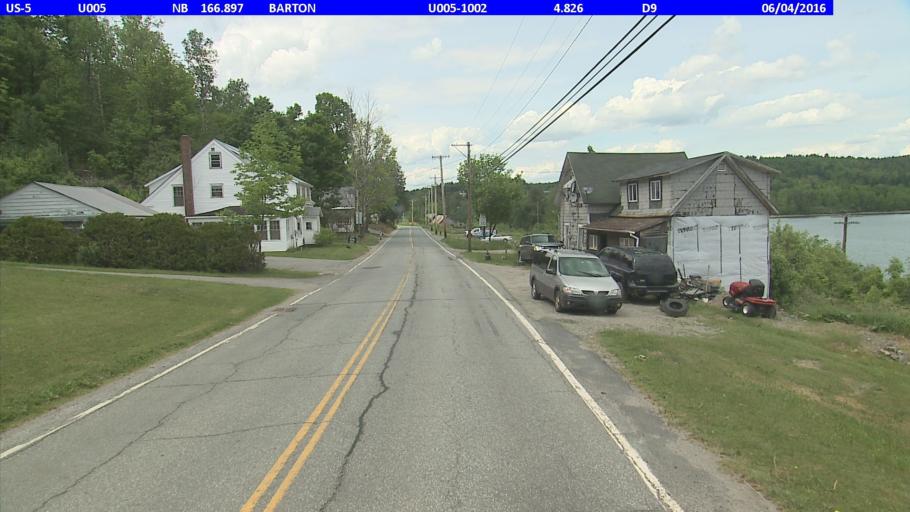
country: US
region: Vermont
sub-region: Orleans County
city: Newport
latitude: 44.7416
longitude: -72.1693
